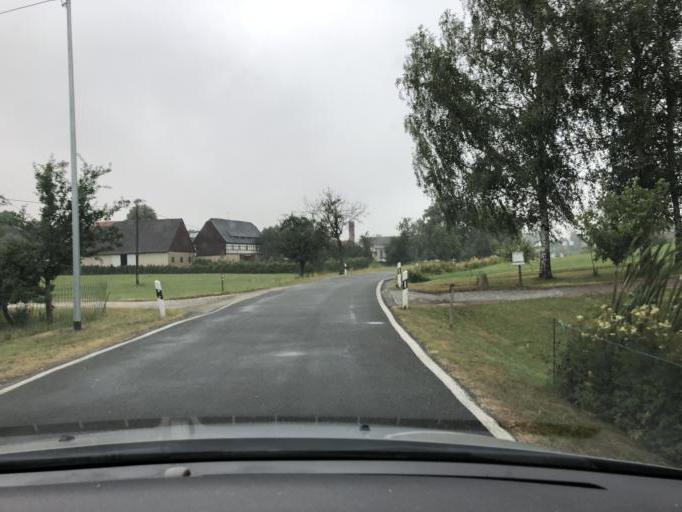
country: DE
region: Saxony
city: Narsdorf
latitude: 50.9937
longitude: 12.6823
